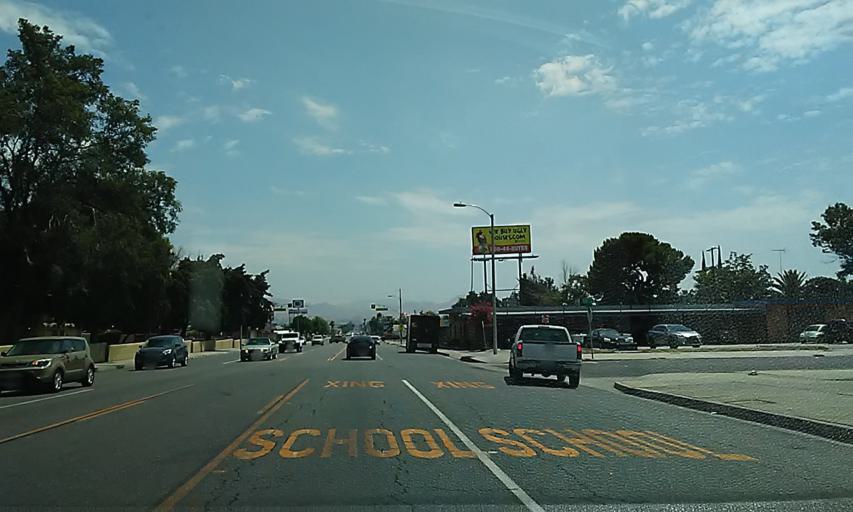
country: US
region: California
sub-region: San Bernardino County
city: San Bernardino
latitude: 34.1199
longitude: -117.2788
